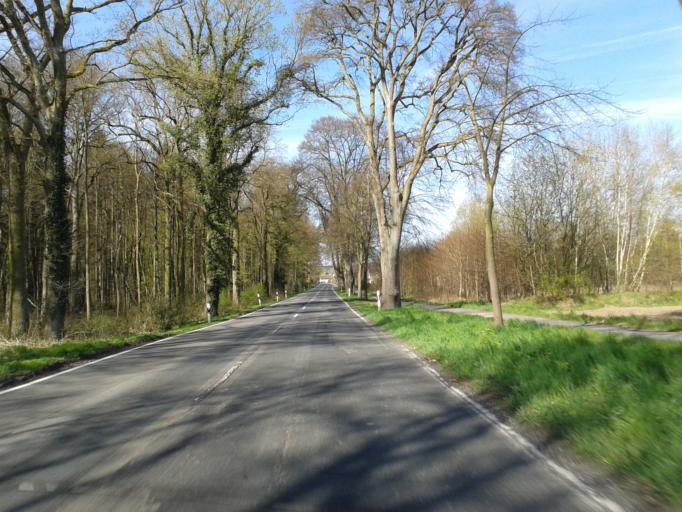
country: DE
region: Lower Saxony
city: Clenze
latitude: 52.9366
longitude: 10.9662
